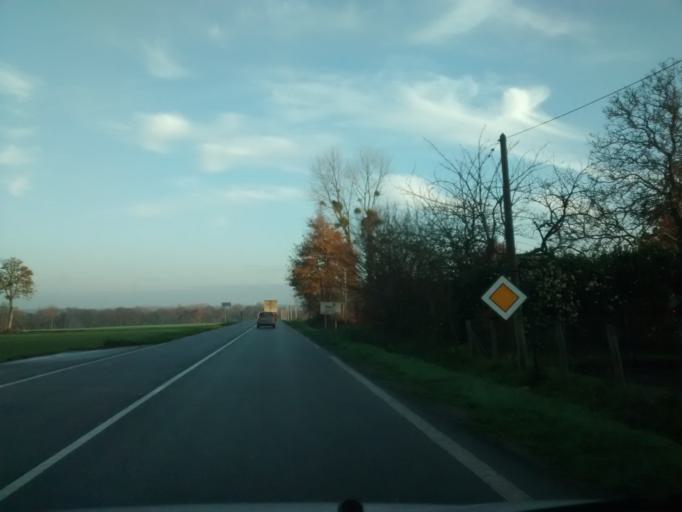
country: FR
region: Brittany
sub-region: Departement d'Ille-et-Vilaine
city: Tremblay
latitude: 48.3912
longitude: -1.4876
